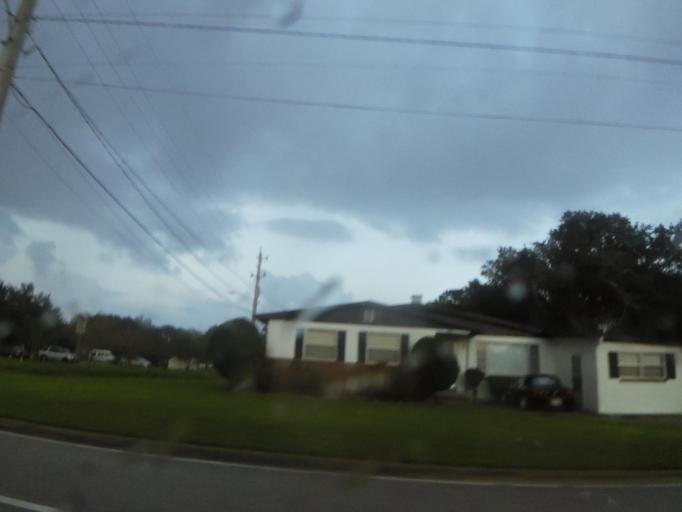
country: US
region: Florida
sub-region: Duval County
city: Jacksonville
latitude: 30.2490
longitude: -81.6224
